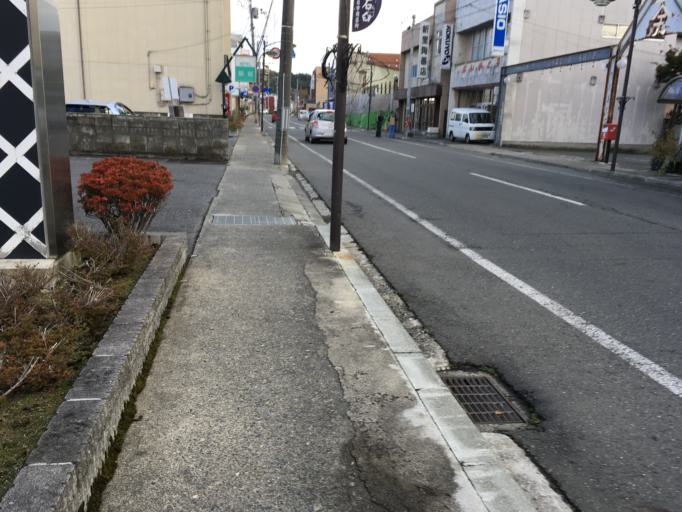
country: JP
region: Iwate
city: Tono
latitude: 39.3293
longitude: 141.5306
